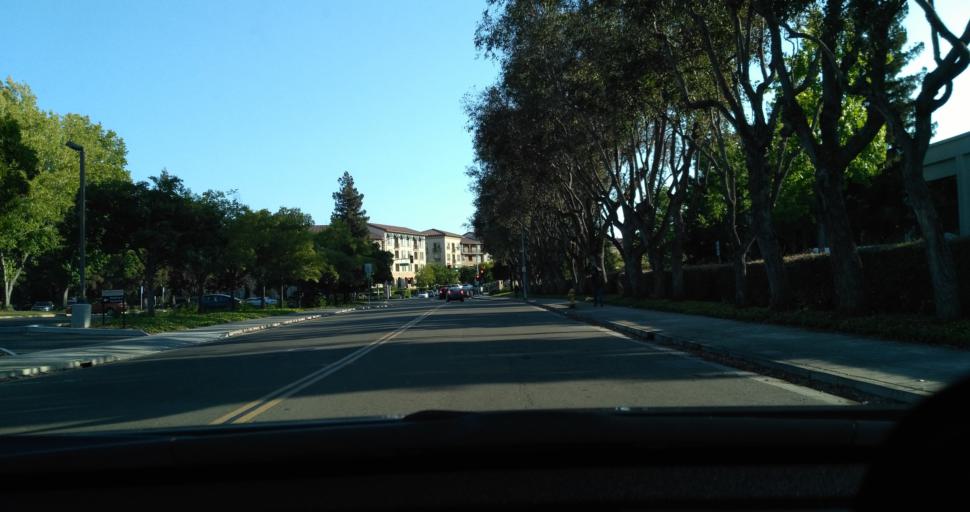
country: US
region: California
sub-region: Santa Clara County
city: Milpitas
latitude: 37.4052
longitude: -121.9287
